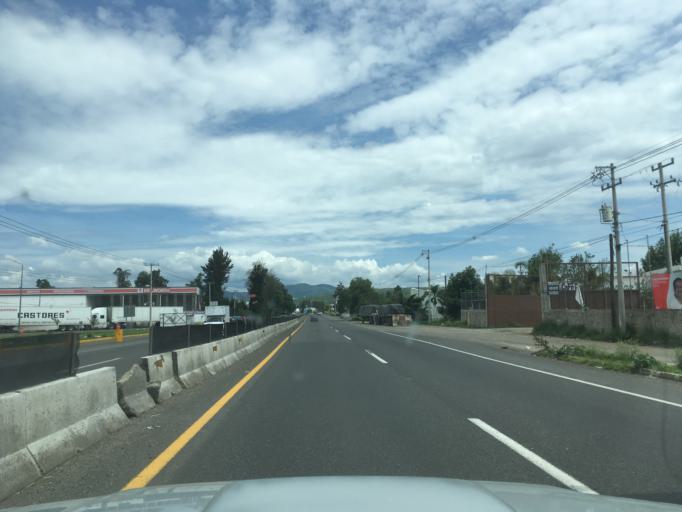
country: MX
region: Michoacan
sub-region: Tarimbaro
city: San Pedro de los Sauces
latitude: 19.7890
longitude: -101.1599
